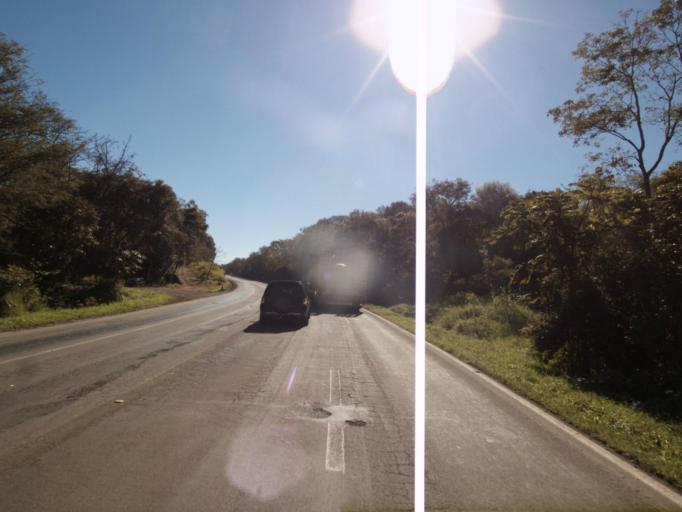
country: AR
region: Misiones
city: Bernardo de Irigoyen
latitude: -26.7755
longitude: -53.4589
